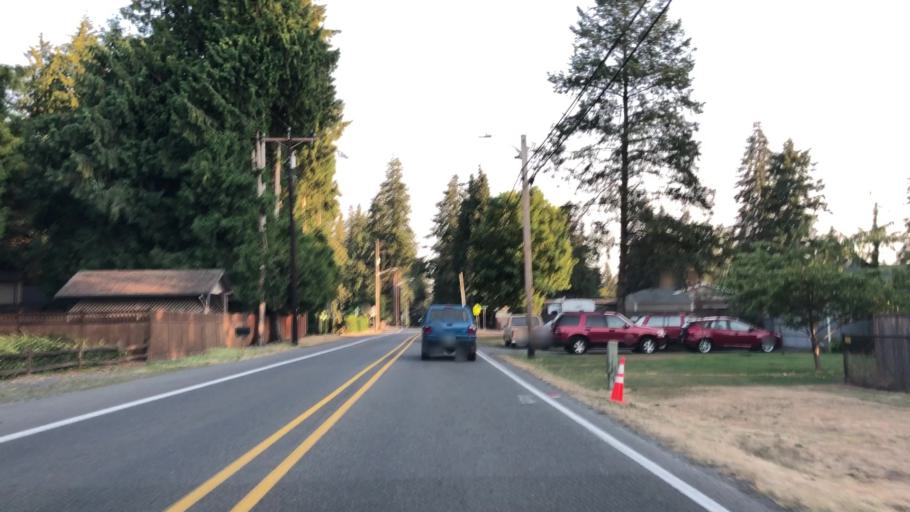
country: US
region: Washington
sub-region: Snohomish County
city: Smokey Point
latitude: 48.1163
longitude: -122.1624
